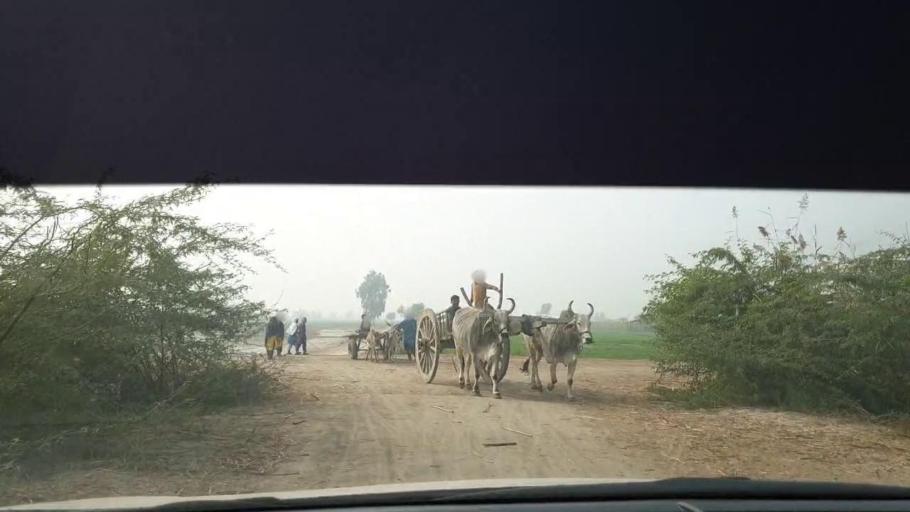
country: PK
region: Sindh
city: Berani
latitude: 25.8307
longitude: 68.8355
